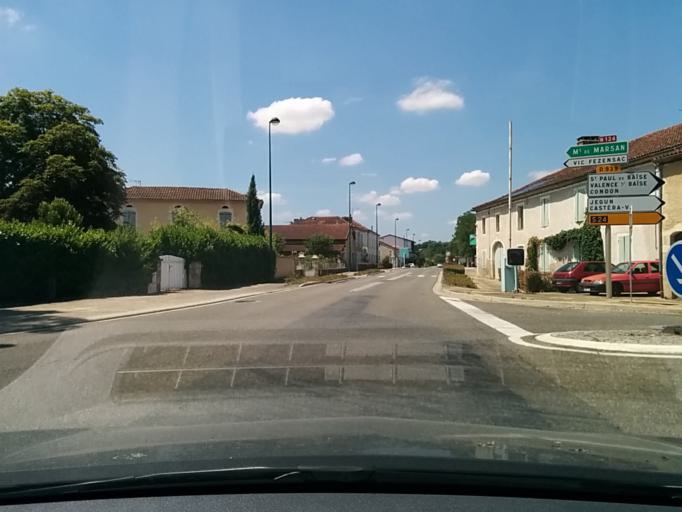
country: FR
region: Midi-Pyrenees
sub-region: Departement du Gers
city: Vic-Fezensac
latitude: 43.7239
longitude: 0.3797
